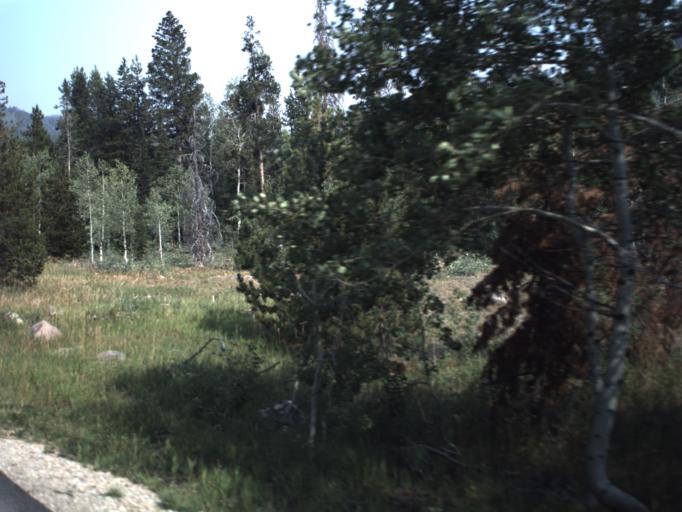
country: US
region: Utah
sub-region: Summit County
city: Francis
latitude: 40.5915
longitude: -111.0141
